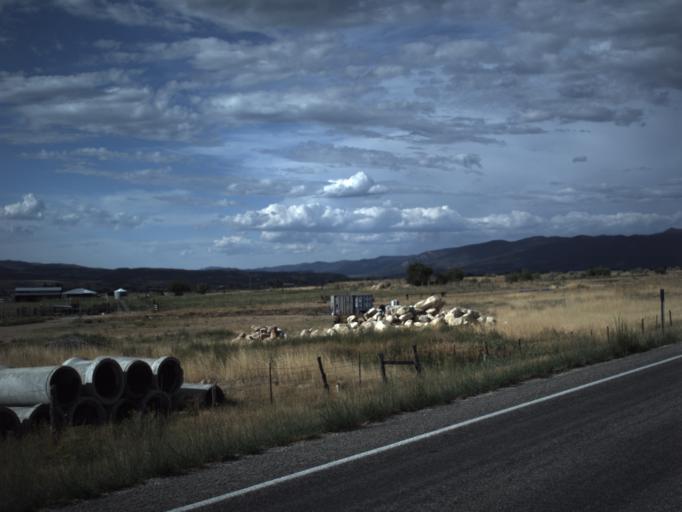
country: US
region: Utah
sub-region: Sanpete County
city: Mount Pleasant
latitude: 39.5196
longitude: -111.4827
